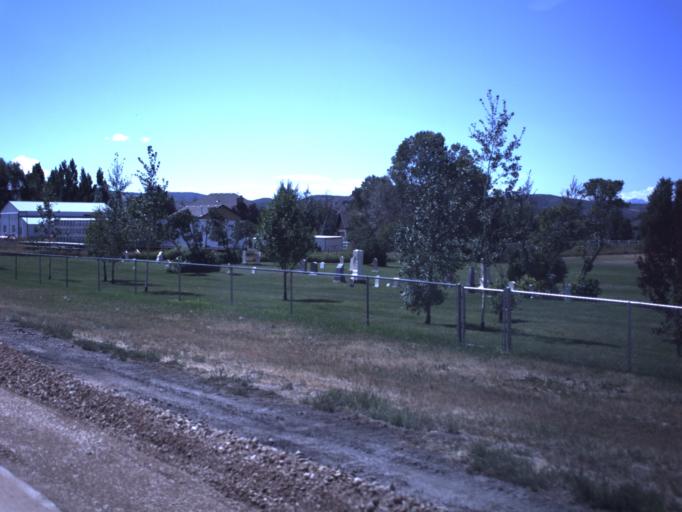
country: US
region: Utah
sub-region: Summit County
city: Francis
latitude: 40.6185
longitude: -111.2807
